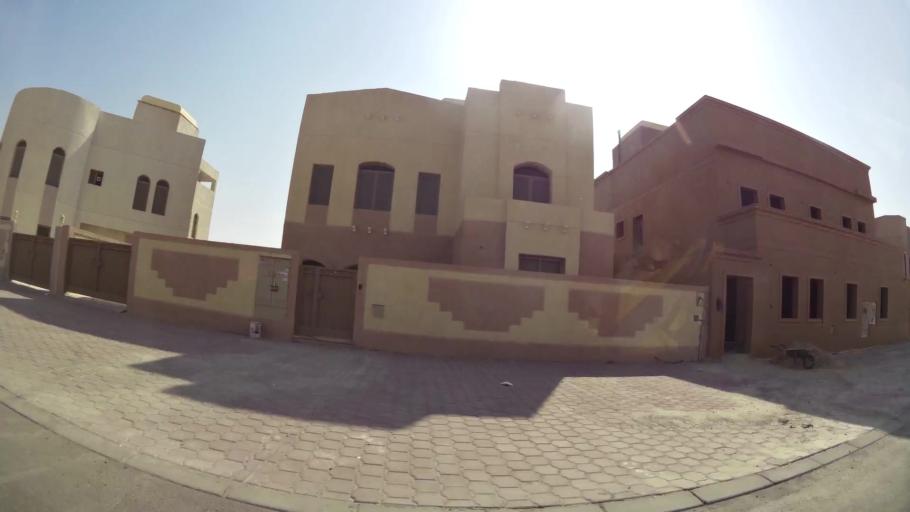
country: KW
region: Al Ahmadi
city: Al Wafrah
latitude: 28.7952
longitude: 48.0772
